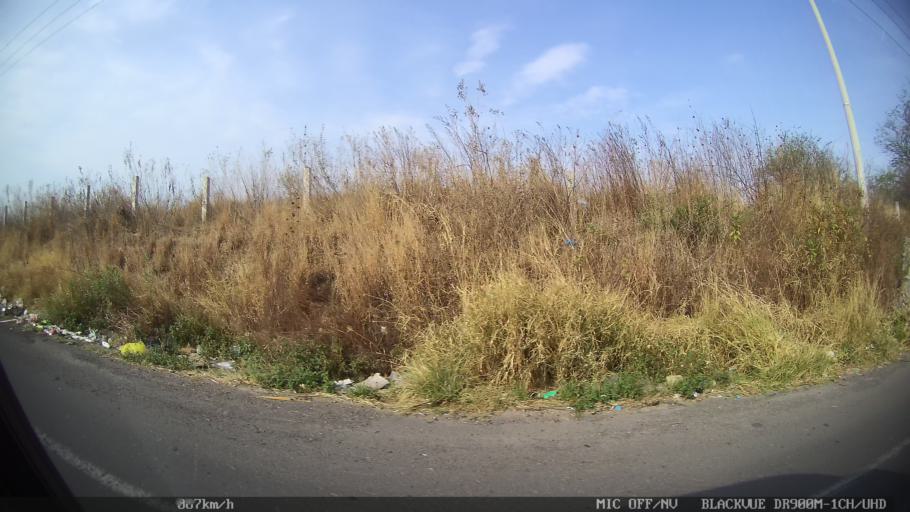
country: MX
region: Jalisco
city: Coyula
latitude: 20.6537
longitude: -103.2088
